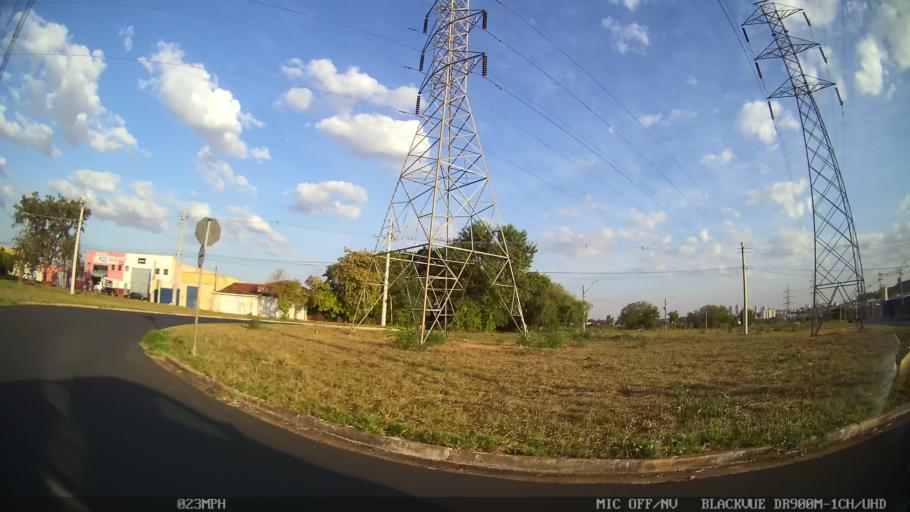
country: BR
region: Sao Paulo
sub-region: Ribeirao Preto
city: Ribeirao Preto
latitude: -21.1679
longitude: -47.7537
